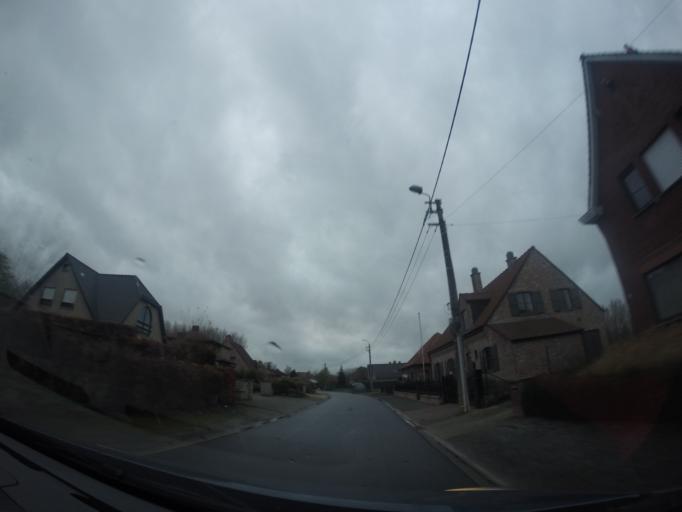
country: BE
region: Flanders
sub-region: Provincie Oost-Vlaanderen
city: Nevele
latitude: 51.0715
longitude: 3.5286
